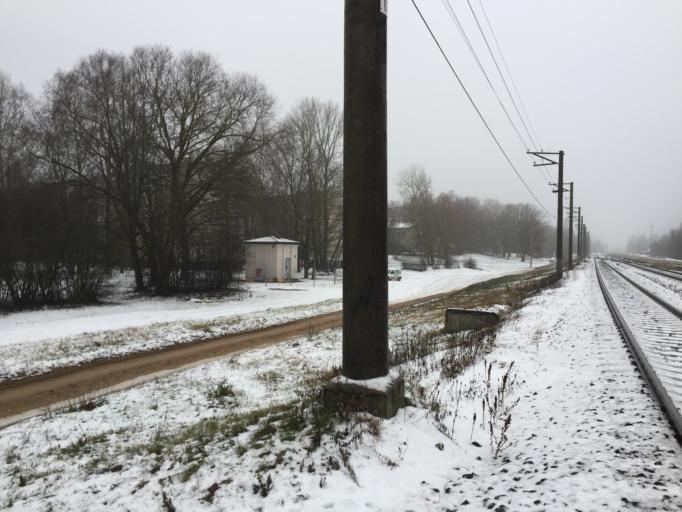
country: LV
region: Riga
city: Jaunciems
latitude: 56.9889
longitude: 24.2207
